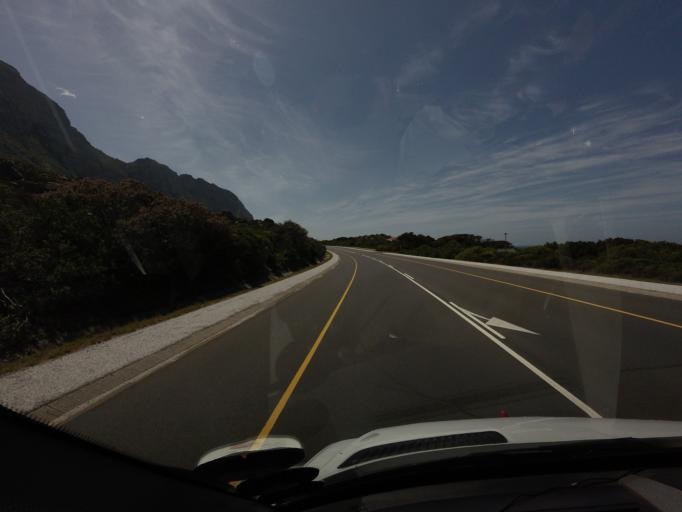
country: ZA
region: Western Cape
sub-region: Overberg District Municipality
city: Grabouw
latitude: -34.3571
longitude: 18.9440
